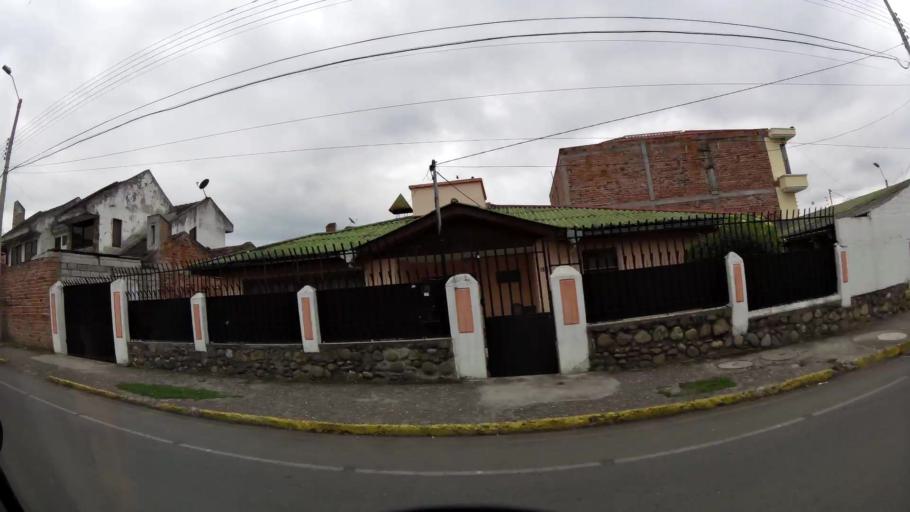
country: EC
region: Azuay
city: Cuenca
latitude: -2.9077
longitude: -79.0193
